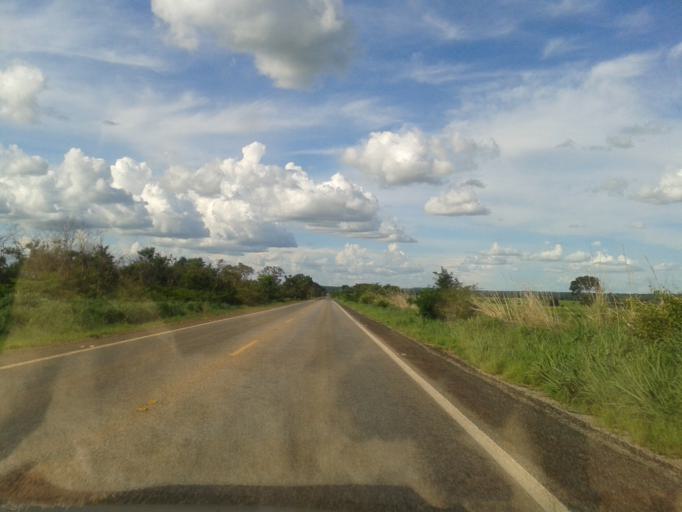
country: BR
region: Goias
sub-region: Mozarlandia
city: Mozarlandia
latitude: -14.5216
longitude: -50.4856
